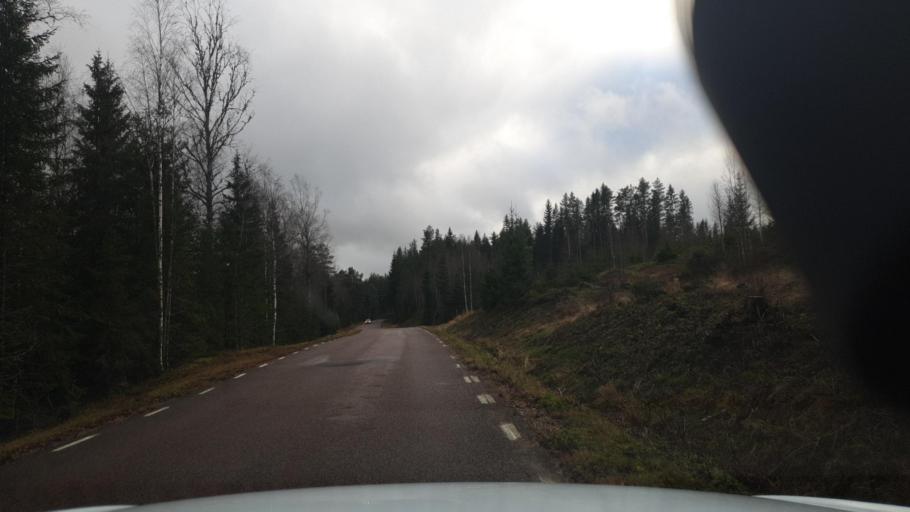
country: SE
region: Vaermland
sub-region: Arvika Kommun
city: Arvika
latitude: 59.8132
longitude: 12.8335
